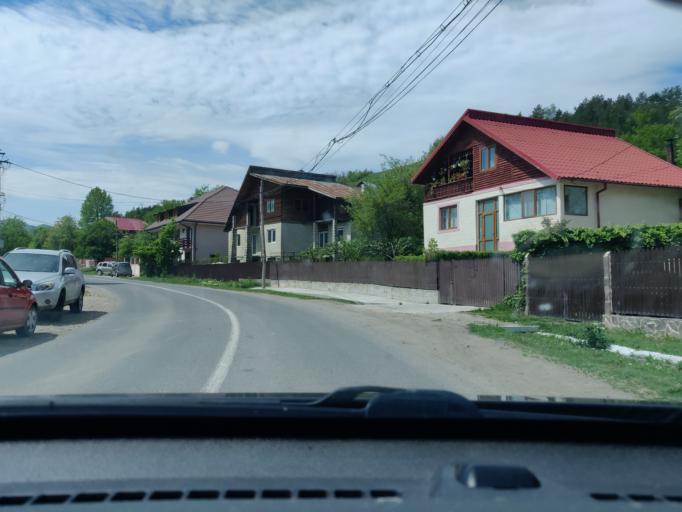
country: RO
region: Vrancea
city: Dragosloveni
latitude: 46.0038
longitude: 26.6702
